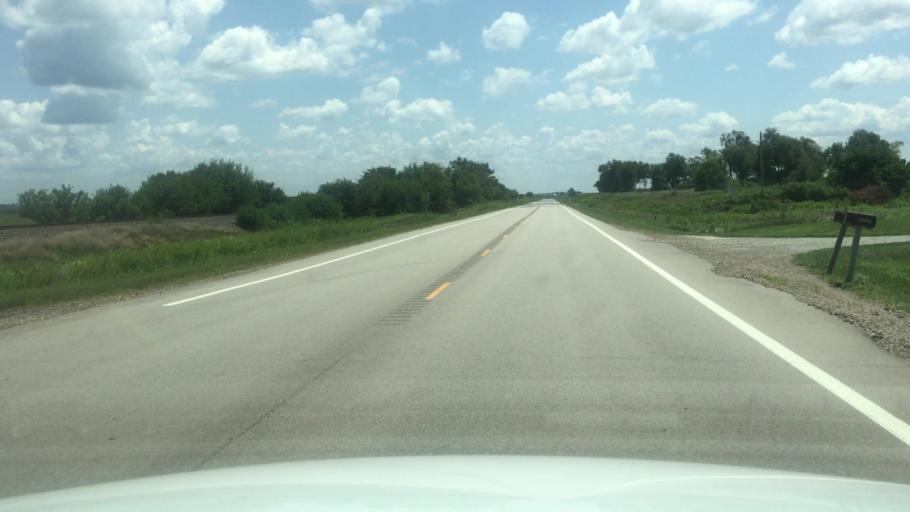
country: US
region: Kansas
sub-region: Brown County
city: Horton
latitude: 39.6050
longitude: -95.3404
